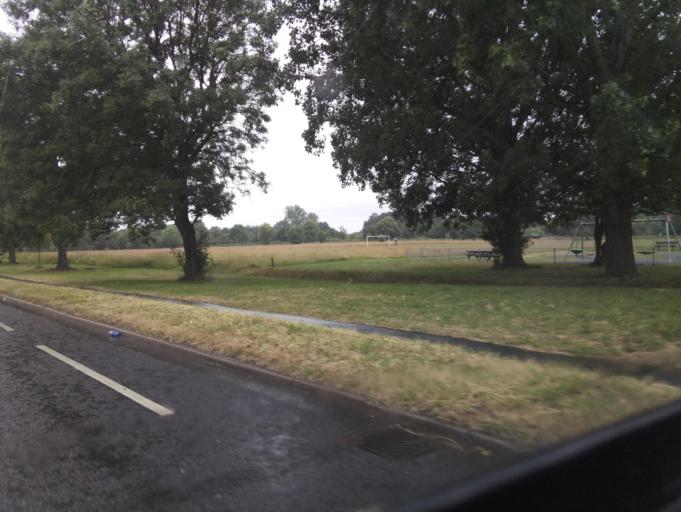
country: GB
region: England
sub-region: Surrey
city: Salfords
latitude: 51.2121
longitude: -0.1698
